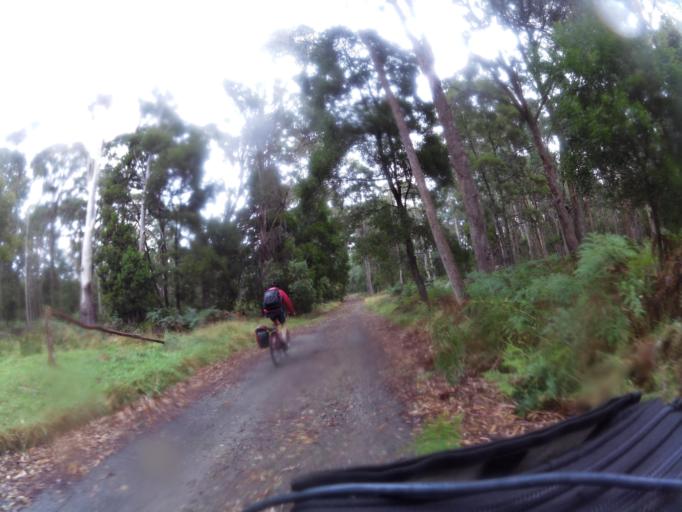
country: AU
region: New South Wales
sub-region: Greater Hume Shire
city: Holbrook
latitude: -36.1913
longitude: 147.5411
